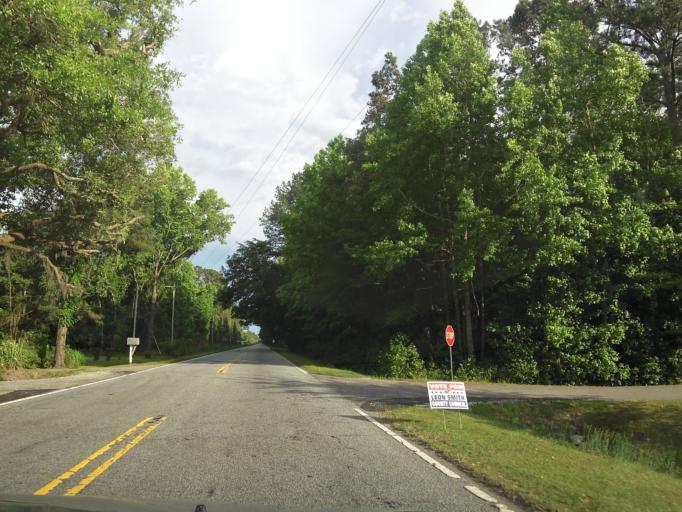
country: US
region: South Carolina
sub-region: Hampton County
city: Estill
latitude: 32.5825
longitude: -81.1945
